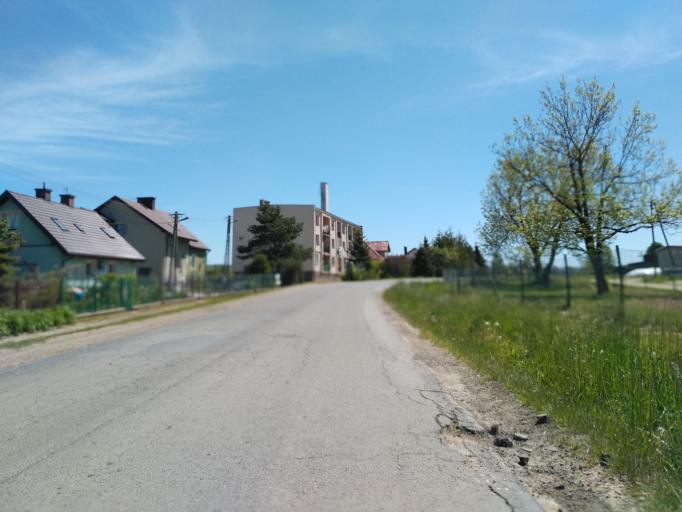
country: PL
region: Subcarpathian Voivodeship
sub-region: Powiat krosnienski
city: Sieniawa
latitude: 49.5406
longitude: 21.9673
